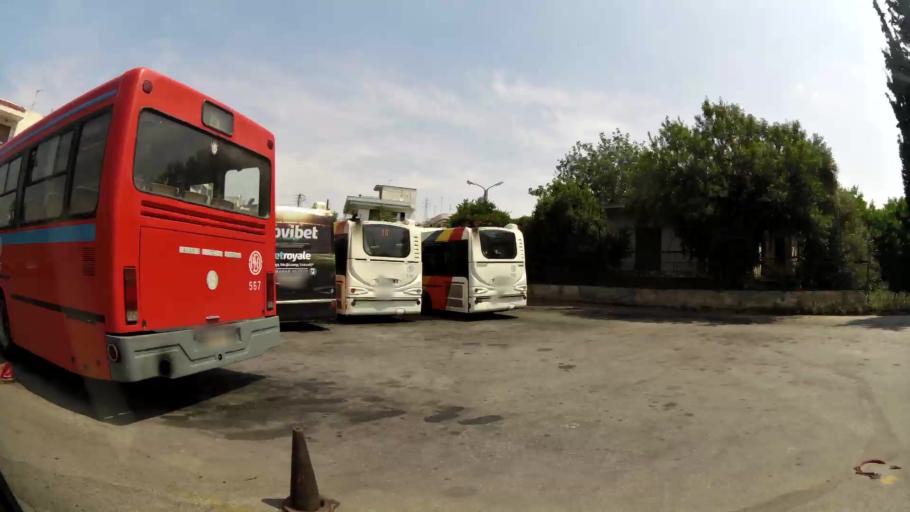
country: GR
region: Central Macedonia
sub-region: Nomos Thessalonikis
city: Agios Pavlos
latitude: 40.6272
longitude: 22.9668
